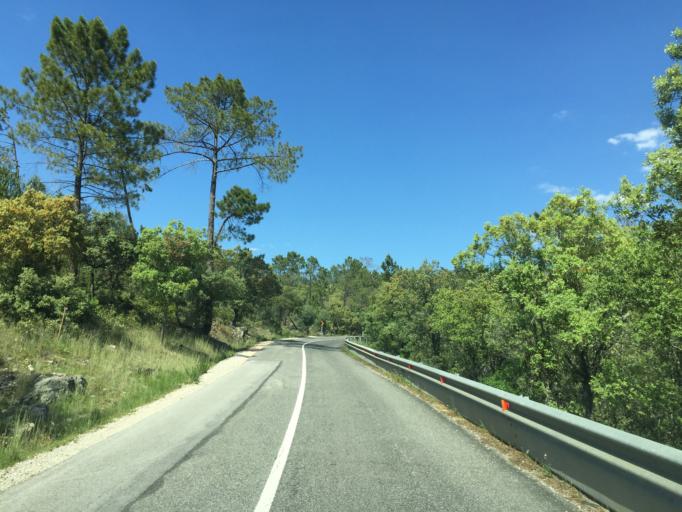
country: PT
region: Leiria
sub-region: Alvaiazere
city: Alvaiazere
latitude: 39.7830
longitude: -8.4469
